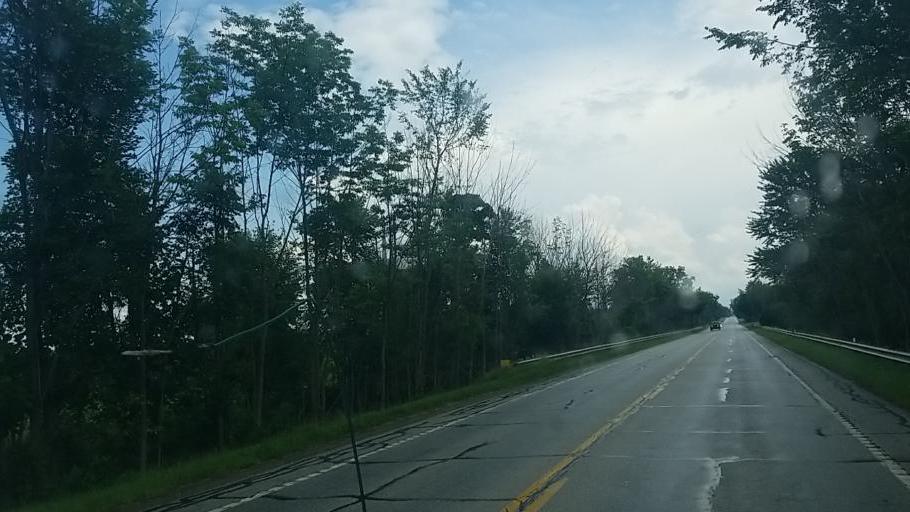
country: US
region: Ohio
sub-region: Lorain County
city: Lagrange
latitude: 41.1680
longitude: -82.0423
